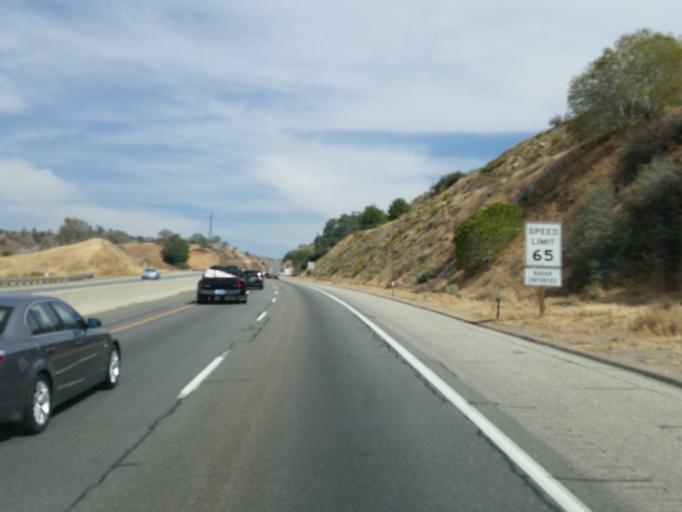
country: US
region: California
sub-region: Kern County
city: Bear Valley Springs
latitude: 35.2603
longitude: -118.6184
